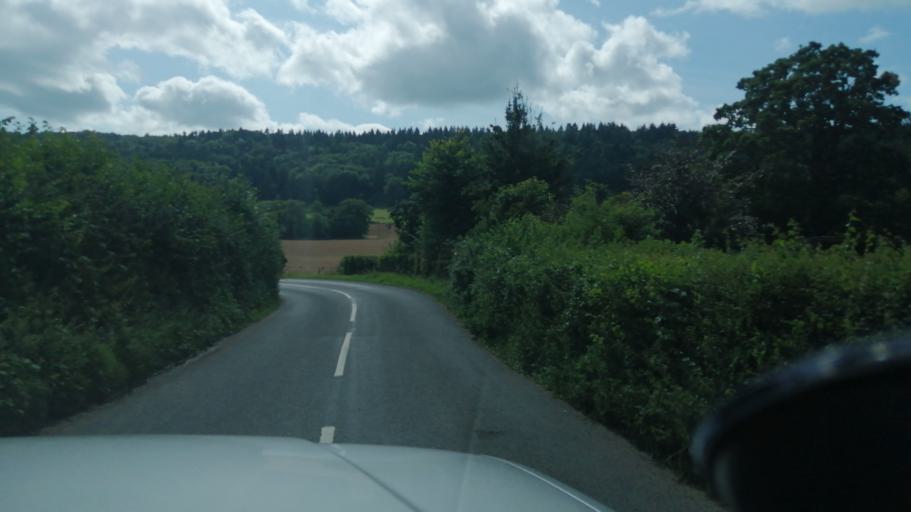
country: GB
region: England
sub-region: Herefordshire
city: Blakemere
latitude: 52.0600
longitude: -2.9284
